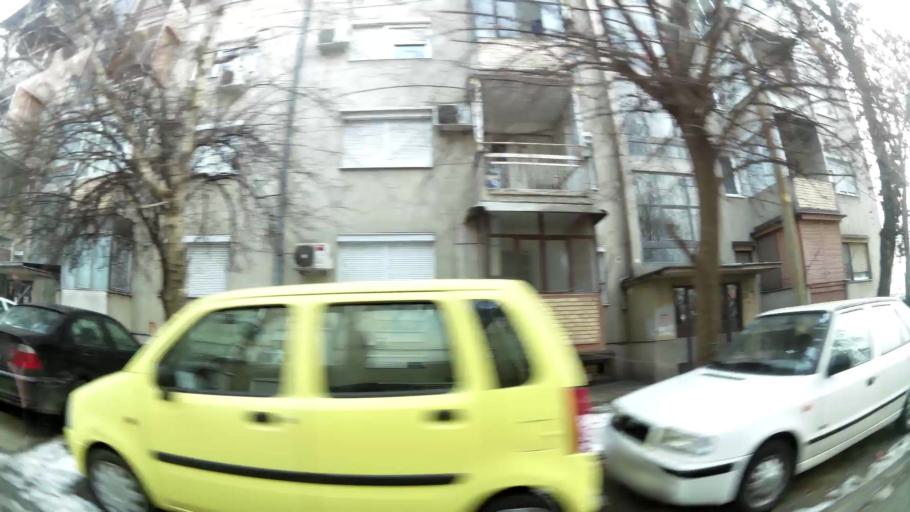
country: MK
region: Kisela Voda
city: Kisela Voda
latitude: 41.9960
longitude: 21.5098
